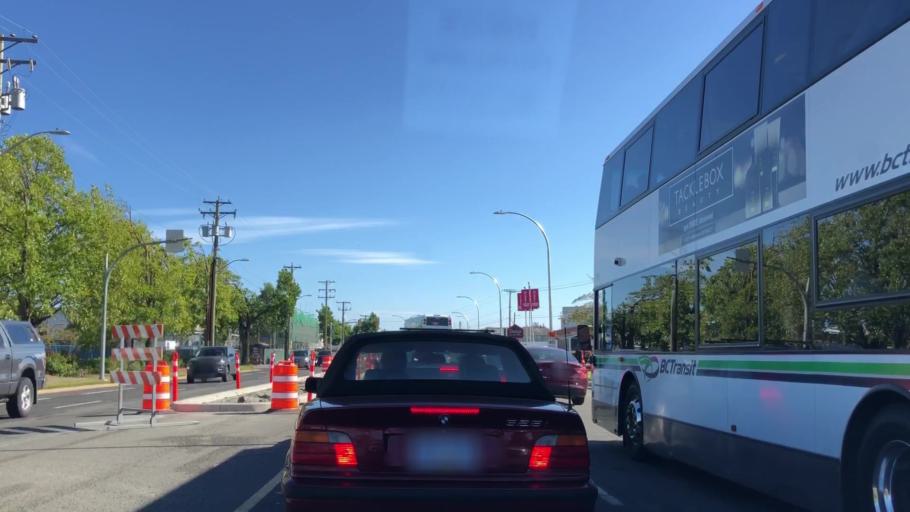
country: CA
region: British Columbia
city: Victoria
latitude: 48.4434
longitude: -123.3698
